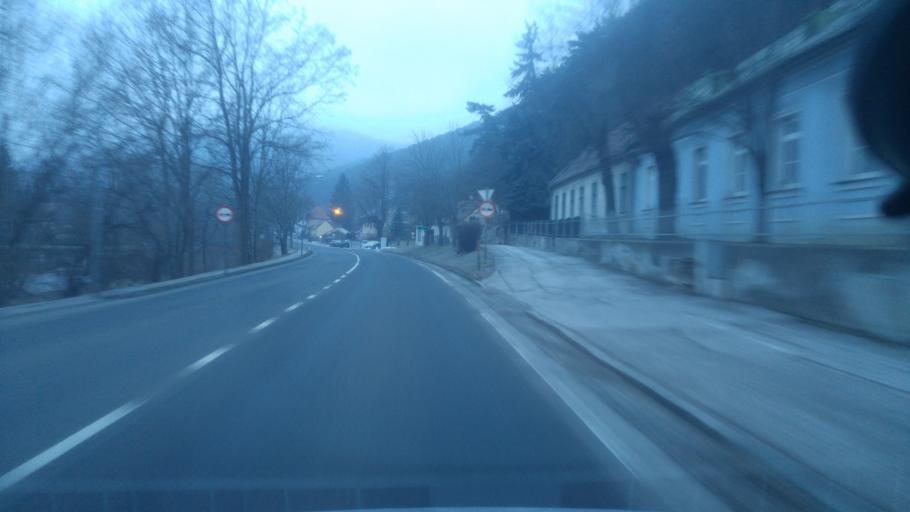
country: AT
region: Lower Austria
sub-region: Politischer Bezirk Baden
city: Weissenbach an der Triesting
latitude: 47.9786
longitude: 16.0683
